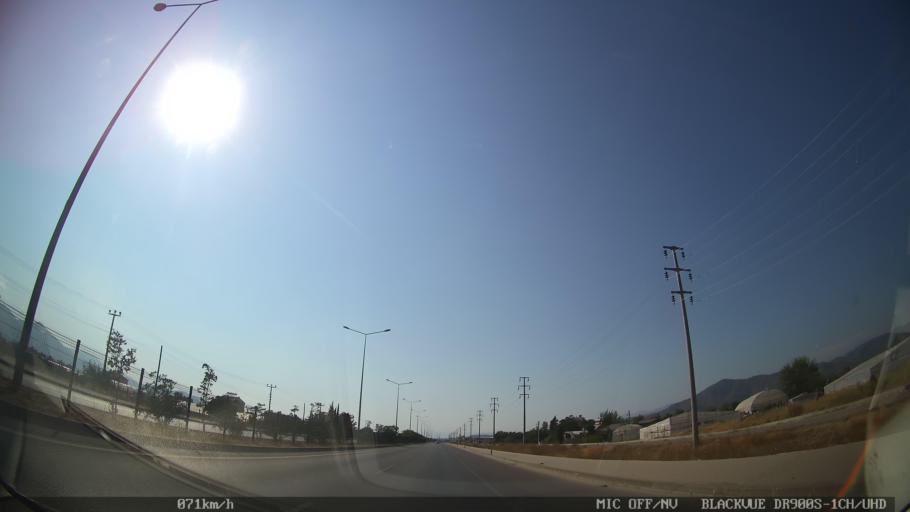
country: TR
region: Mugla
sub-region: Fethiye
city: Fethiye
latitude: 36.6532
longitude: 29.1710
